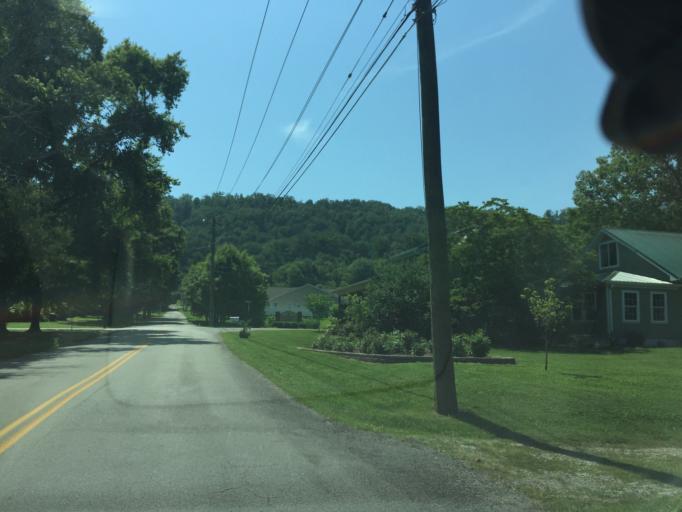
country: US
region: Tennessee
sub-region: Hamilton County
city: Collegedale
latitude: 35.0735
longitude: -85.0578
